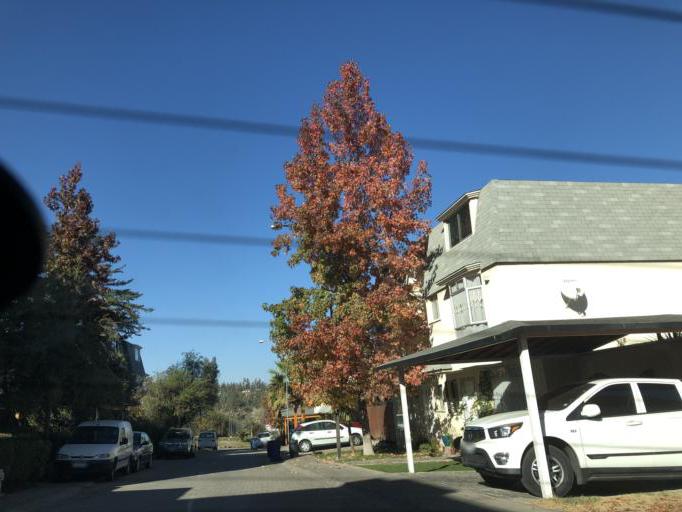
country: CL
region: Santiago Metropolitan
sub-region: Provincia de Cordillera
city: Puente Alto
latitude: -33.5565
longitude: -70.5330
